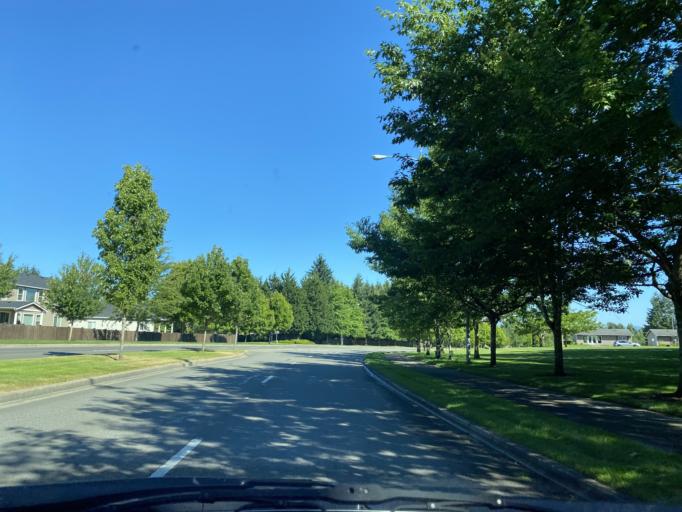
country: US
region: Washington
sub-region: Pierce County
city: McMillin
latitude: 47.1119
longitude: -122.2534
